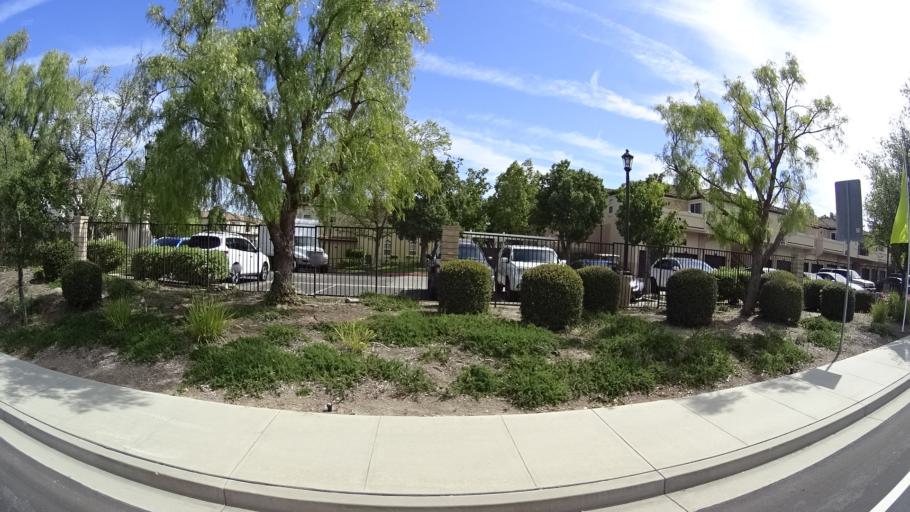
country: US
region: California
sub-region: Ventura County
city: Casa Conejo
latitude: 34.1991
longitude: -118.9233
